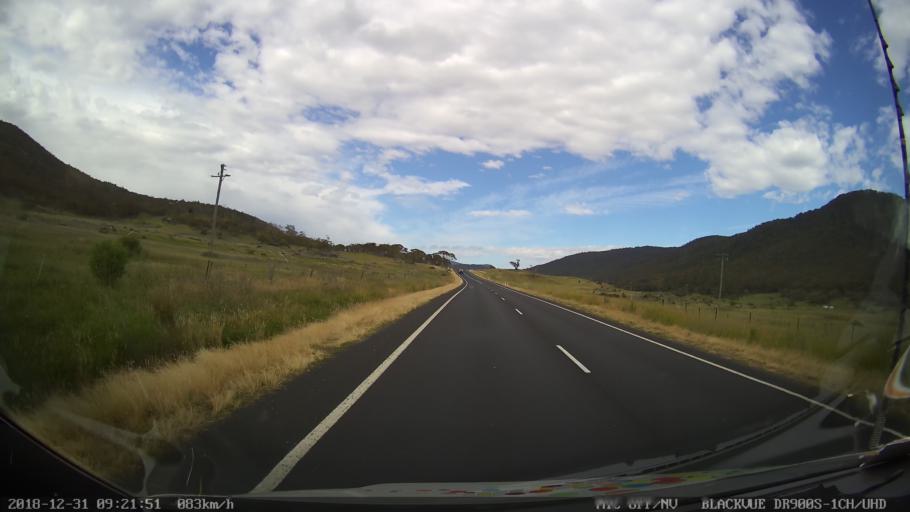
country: AU
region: New South Wales
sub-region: Snowy River
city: Jindabyne
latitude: -36.4314
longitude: 148.5559
